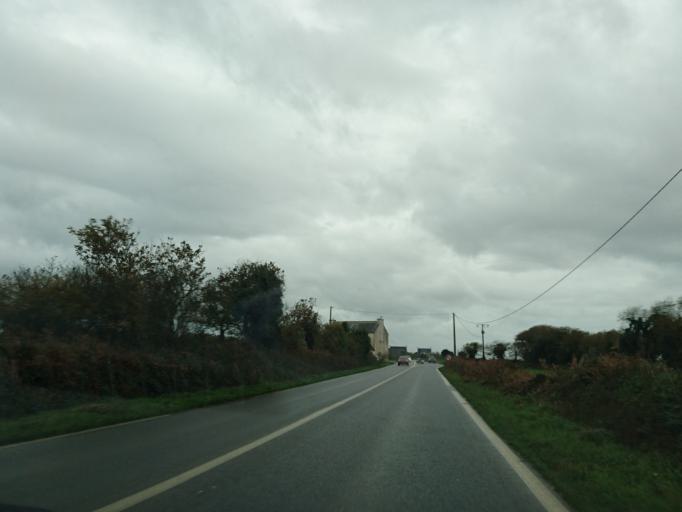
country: FR
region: Brittany
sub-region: Departement du Finistere
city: Plouzane
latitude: 48.3618
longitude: -4.6097
